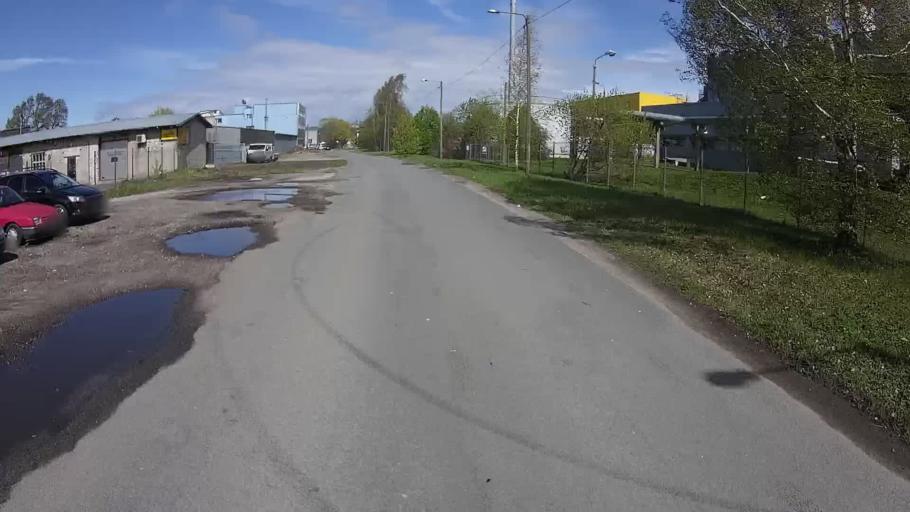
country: EE
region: Harju
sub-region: Tallinna linn
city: Tallinn
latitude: 59.4227
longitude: 24.6910
